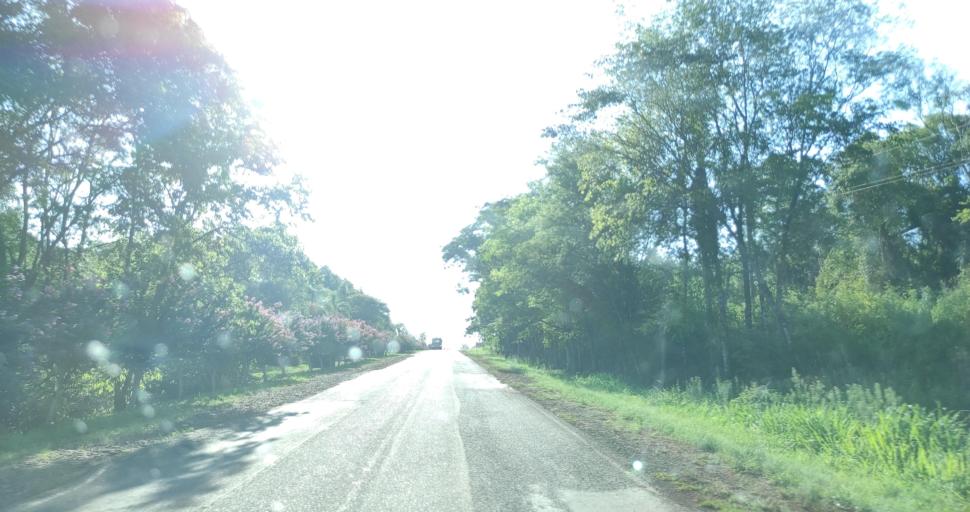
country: AR
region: Misiones
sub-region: Departamento de Eldorado
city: Eldorado
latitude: -26.4059
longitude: -54.4398
